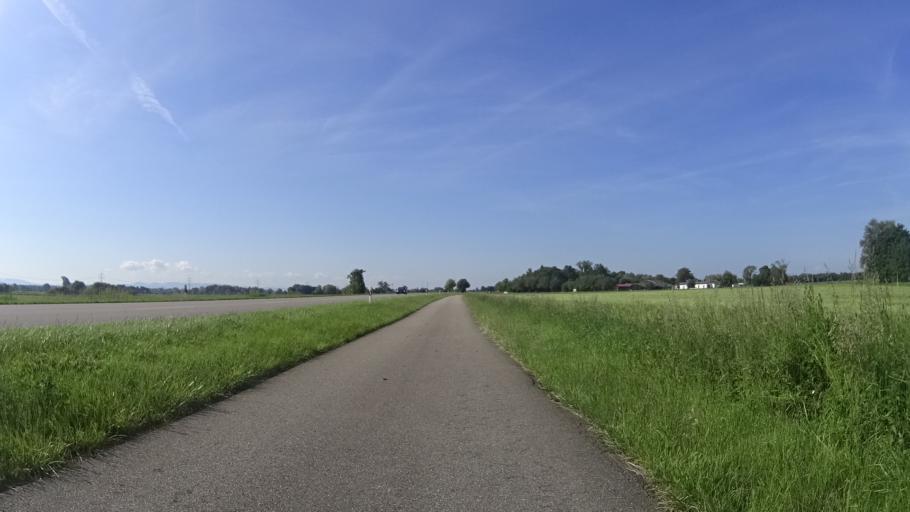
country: DE
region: Baden-Wuerttemberg
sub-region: Freiburg Region
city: Kehl
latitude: 48.5419
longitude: 7.8340
